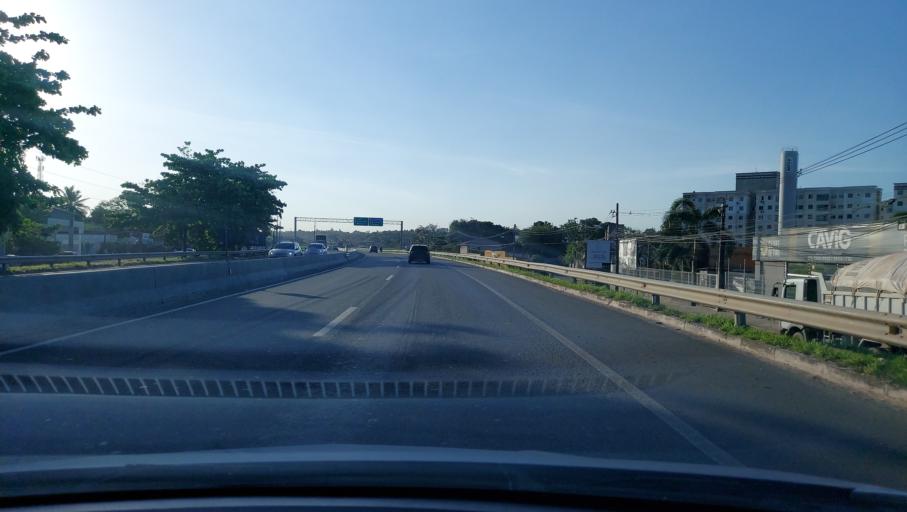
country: BR
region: Bahia
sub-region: Lauro De Freitas
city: Lauro de Freitas
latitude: -12.9031
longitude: -38.3578
